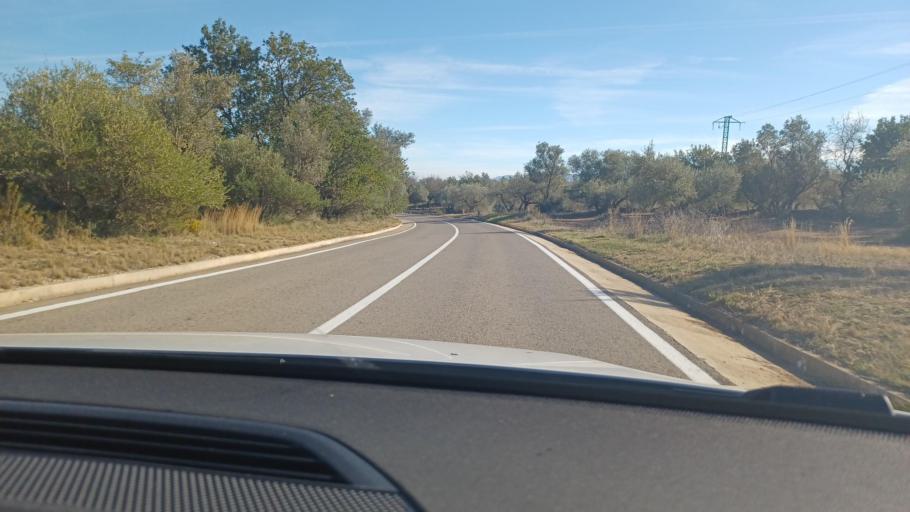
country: ES
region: Catalonia
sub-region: Provincia de Tarragona
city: Mas de Barberans
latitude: 40.7275
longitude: 0.3836
